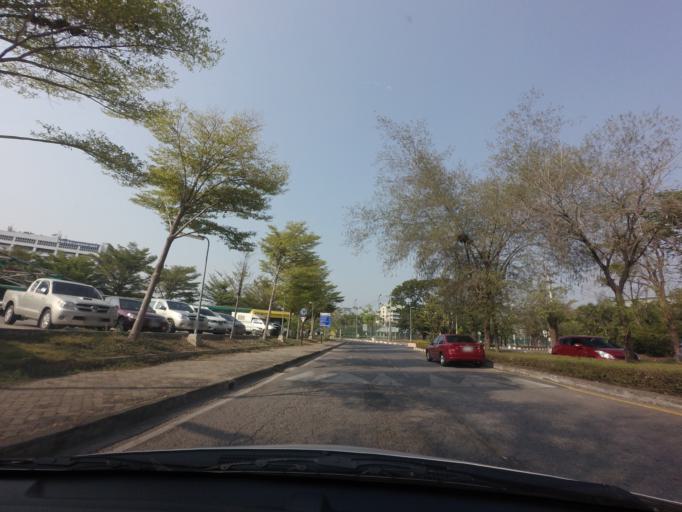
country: TH
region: Nakhon Pathom
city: Salaya
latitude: 13.7964
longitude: 100.3179
